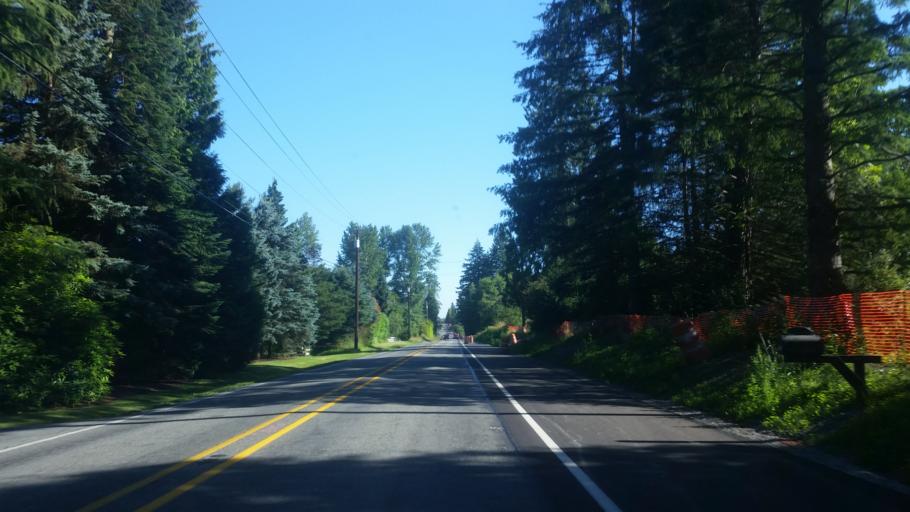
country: US
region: Washington
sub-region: Snohomish County
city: Clearview
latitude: 47.8240
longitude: -122.1097
